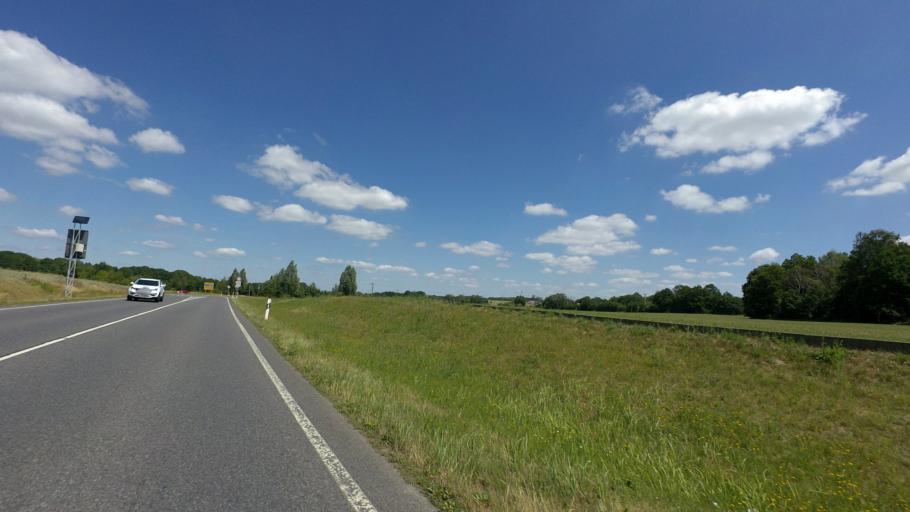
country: DE
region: Brandenburg
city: Luckau
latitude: 51.8412
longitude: 13.6772
